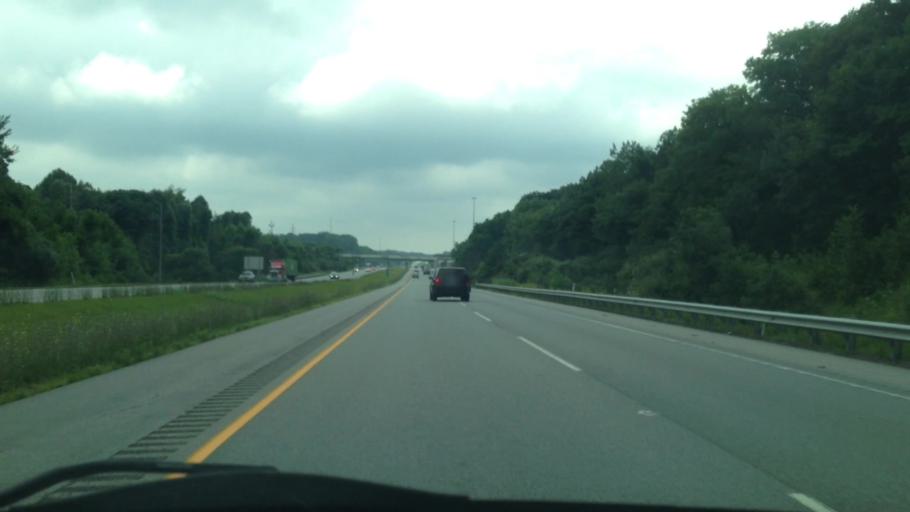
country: US
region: Indiana
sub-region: LaPorte County
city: Westville
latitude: 41.5917
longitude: -86.8911
